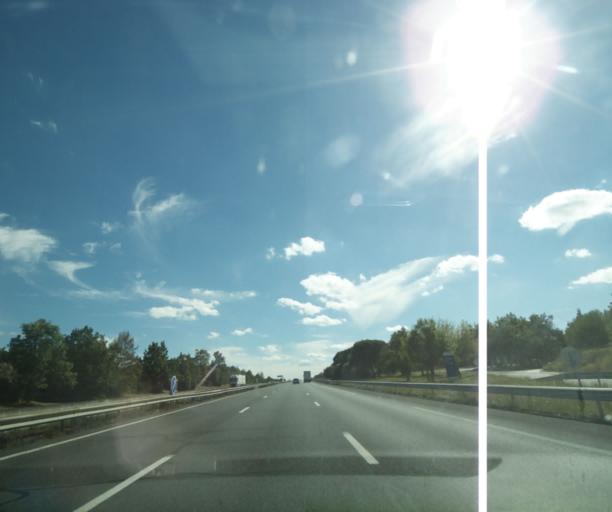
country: FR
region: Midi-Pyrenees
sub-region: Departement du Tarn-et-Garonne
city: Campsas
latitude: 43.8885
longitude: 1.3172
